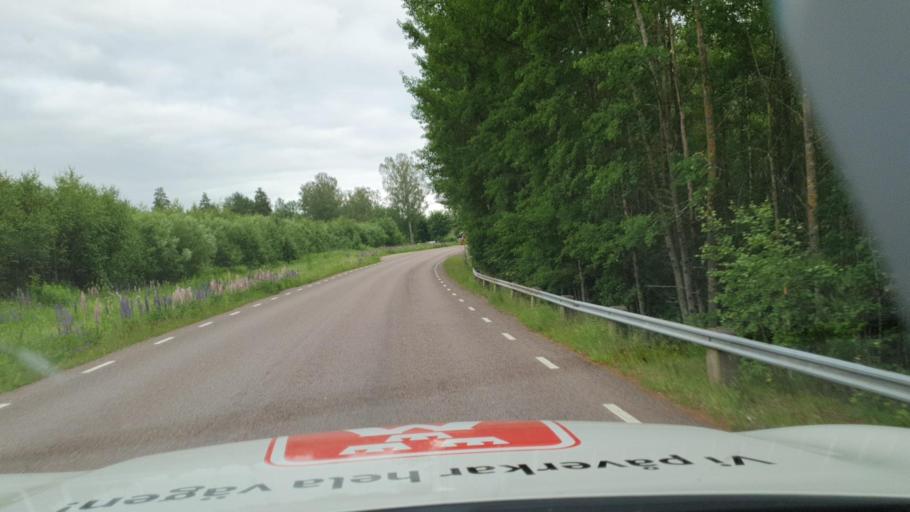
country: SE
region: Vaermland
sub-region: Forshaga Kommun
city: Forshaga
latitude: 59.4995
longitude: 13.4004
